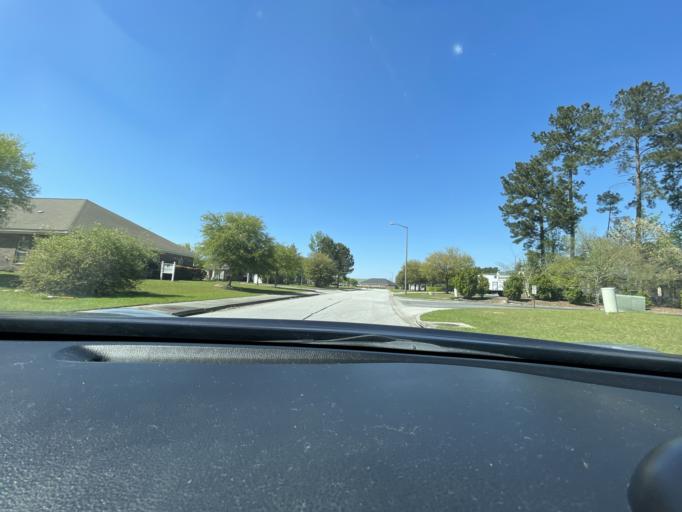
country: US
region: Georgia
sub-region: Chatham County
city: Pooler
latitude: 32.1311
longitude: -81.2533
